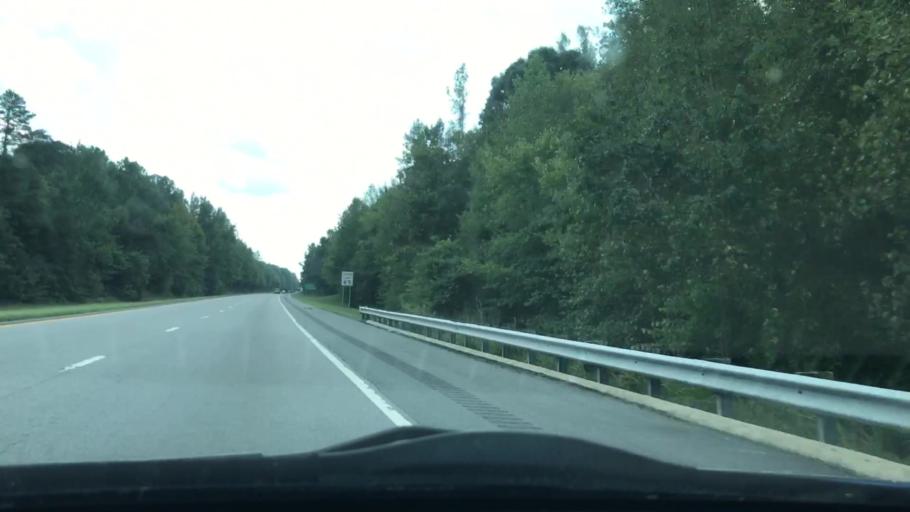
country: US
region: North Carolina
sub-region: Guilford County
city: Pleasant Garden
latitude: 35.9145
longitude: -79.8236
